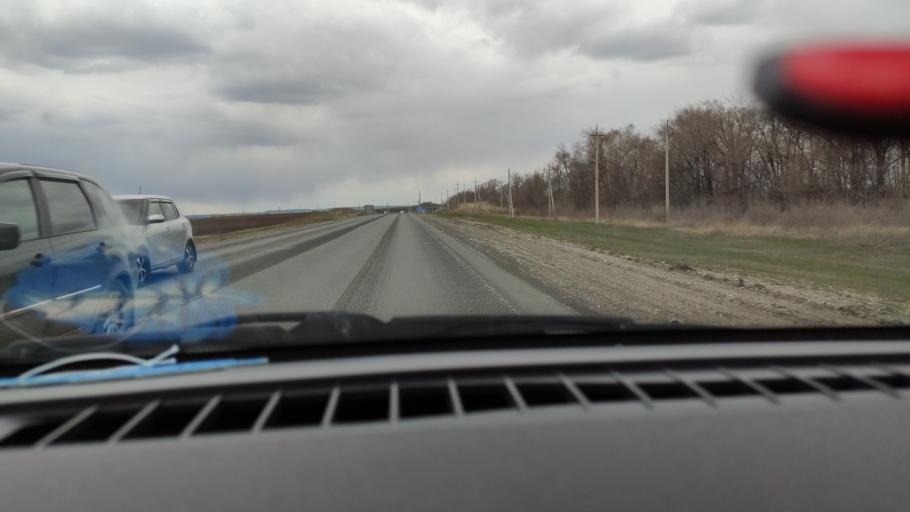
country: RU
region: Saratov
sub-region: Saratovskiy Rayon
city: Saratov
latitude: 51.7750
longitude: 46.0941
